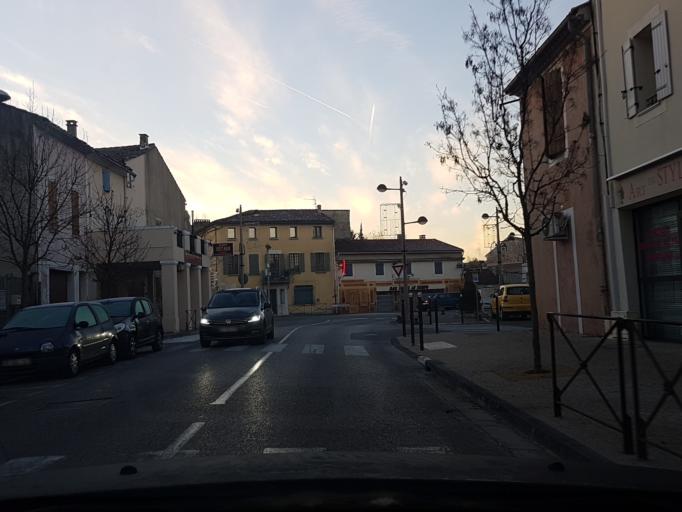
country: FR
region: Provence-Alpes-Cote d'Azur
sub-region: Departement du Vaucluse
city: Monteux
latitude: 44.0353
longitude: 4.9993
